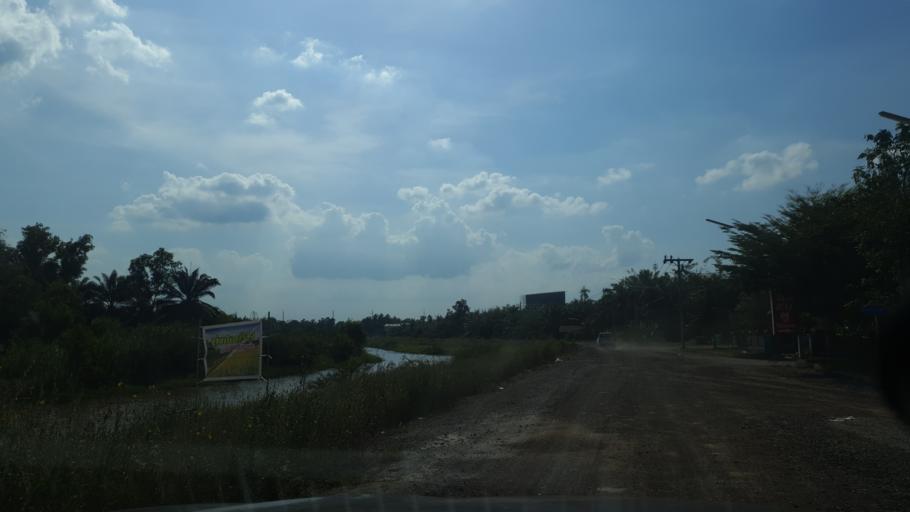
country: TH
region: Surat Thani
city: Phunphin
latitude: 9.1449
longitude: 99.1613
